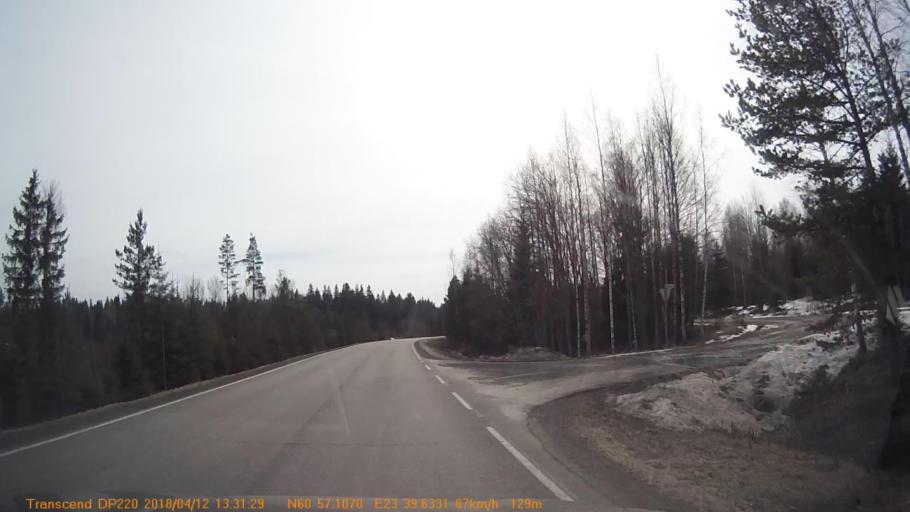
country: FI
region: Haeme
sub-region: Forssa
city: Forssa
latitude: 60.9515
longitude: 23.6606
